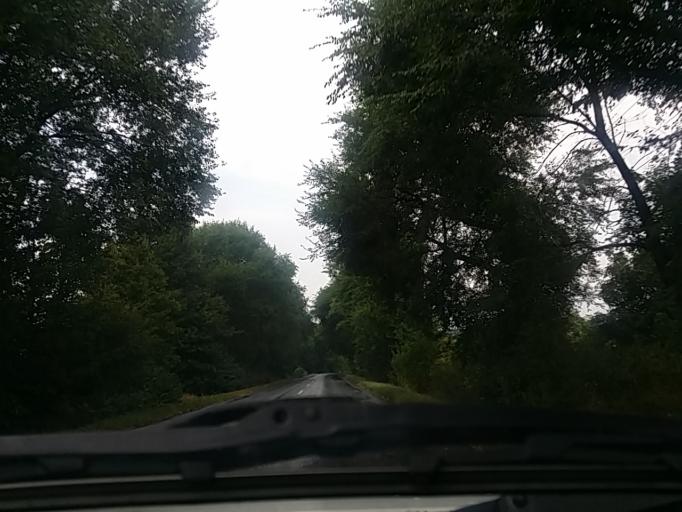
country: HU
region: Pest
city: Zsambek
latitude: 47.5431
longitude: 18.7372
